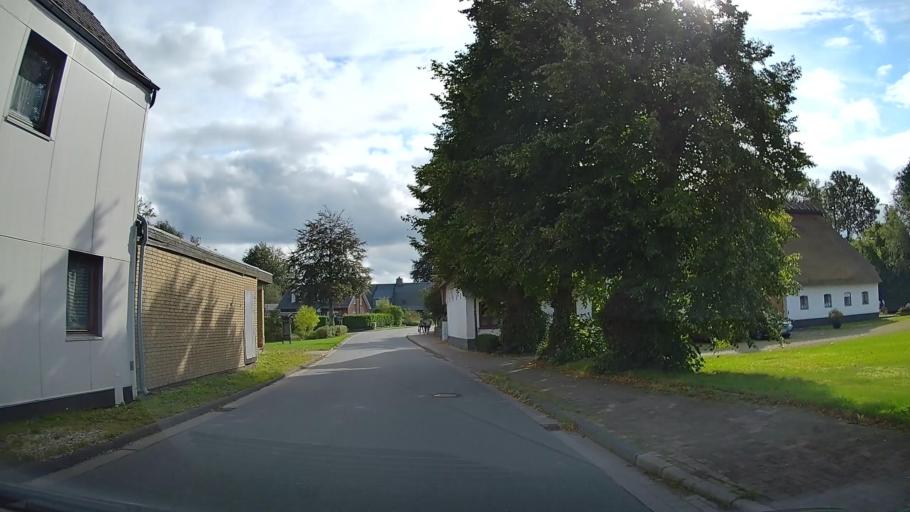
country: DE
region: Schleswig-Holstein
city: Ringsberg
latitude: 54.8066
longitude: 9.5985
